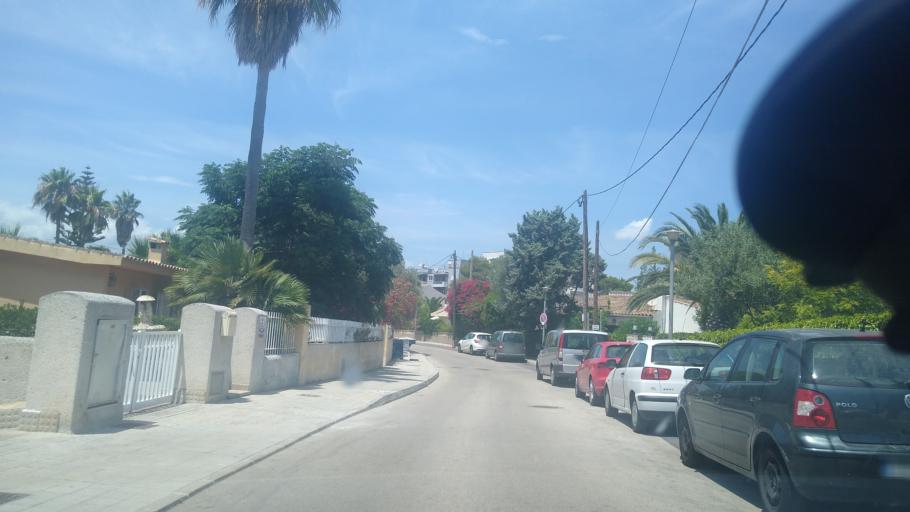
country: ES
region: Balearic Islands
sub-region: Illes Balears
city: Santa Margalida
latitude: 39.7585
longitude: 3.1649
